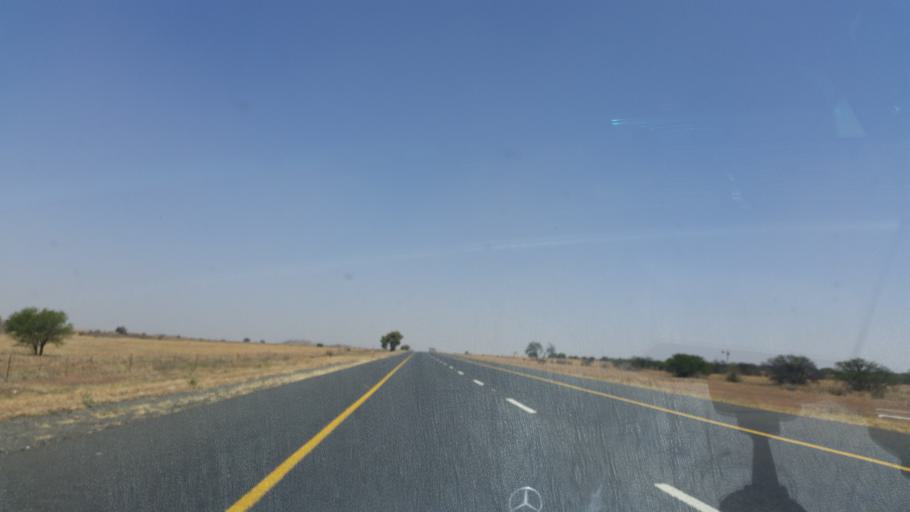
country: ZA
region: Orange Free State
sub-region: Lejweleputswa District Municipality
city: Winburg
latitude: -28.6762
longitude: 26.8367
